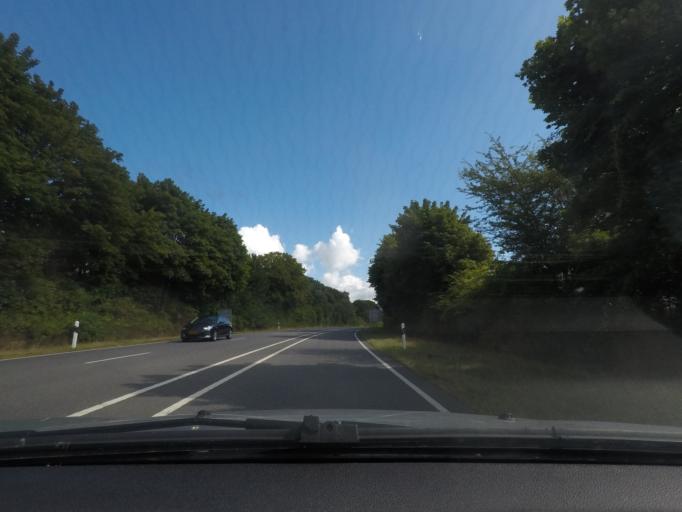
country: LU
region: Grevenmacher
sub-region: Canton de Grevenmacher
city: Junglinster
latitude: 49.7230
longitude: 6.2746
